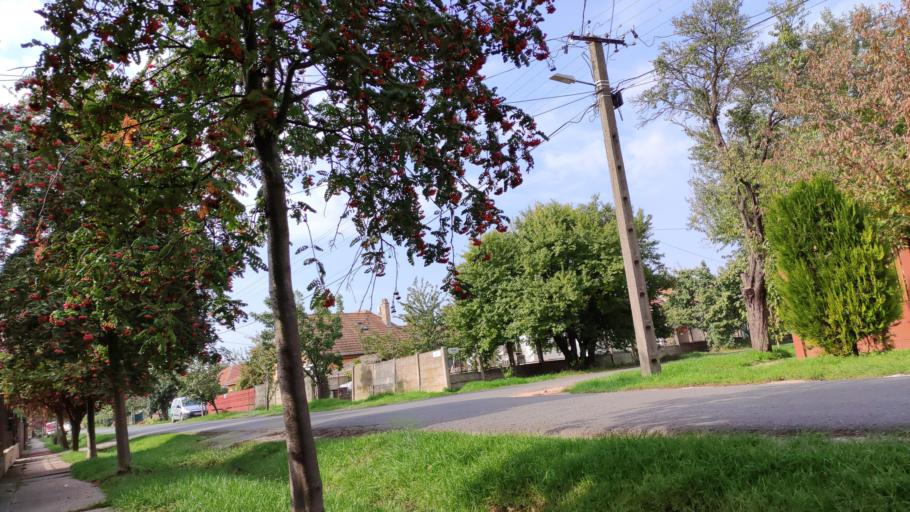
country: HU
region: Hajdu-Bihar
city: Hajduboszormeny
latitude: 47.6842
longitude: 21.5041
